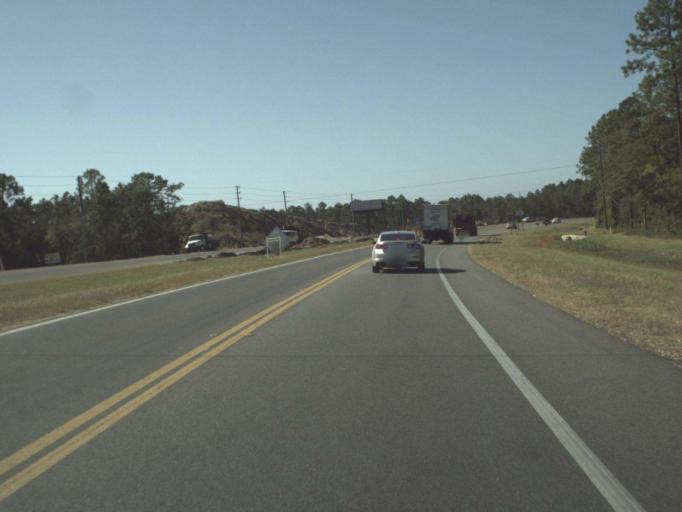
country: US
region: Florida
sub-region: Walton County
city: Freeport
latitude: 30.4478
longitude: -86.1332
